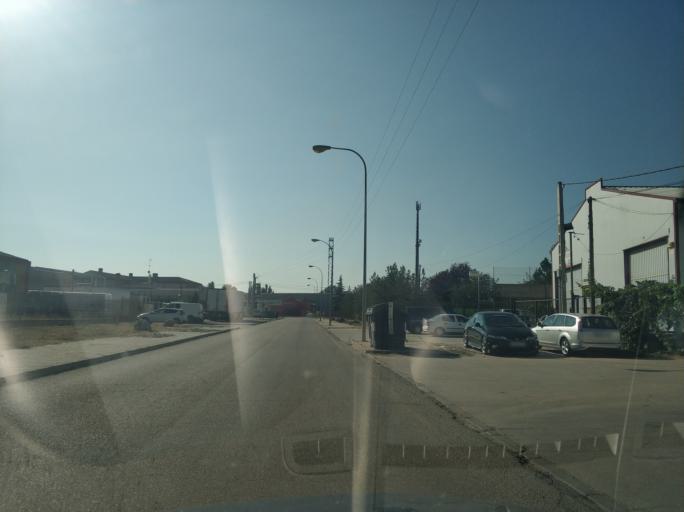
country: ES
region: Castille and Leon
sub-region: Provincia de Burgos
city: Aranda de Duero
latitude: 41.6681
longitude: -3.7097
